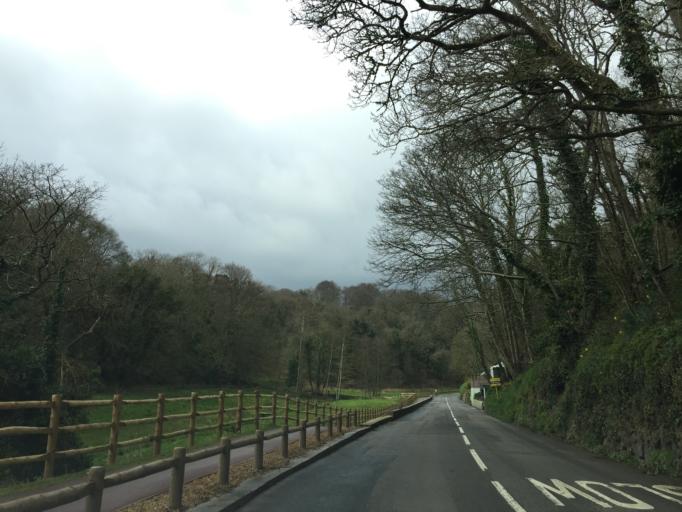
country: JE
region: St Helier
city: Saint Helier
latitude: 49.2124
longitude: -2.1680
